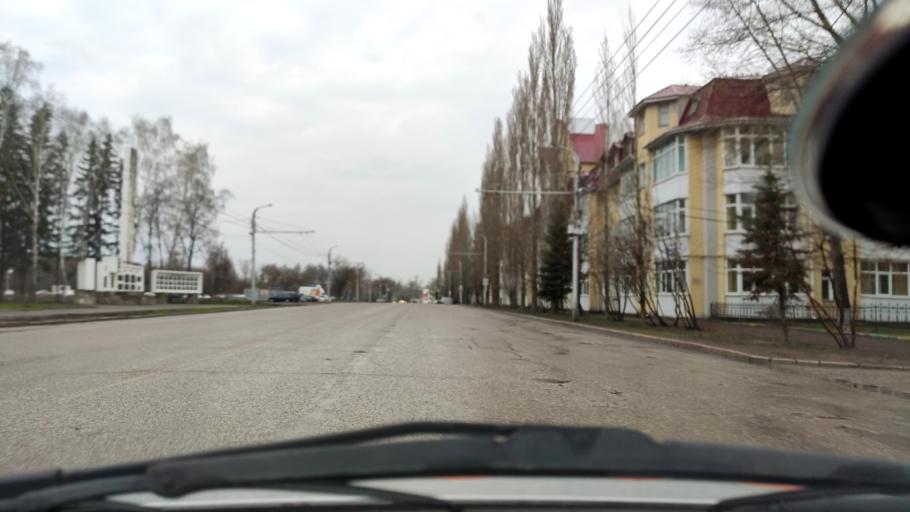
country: RU
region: Bashkortostan
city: Sterlitamak
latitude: 53.6506
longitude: 55.9463
